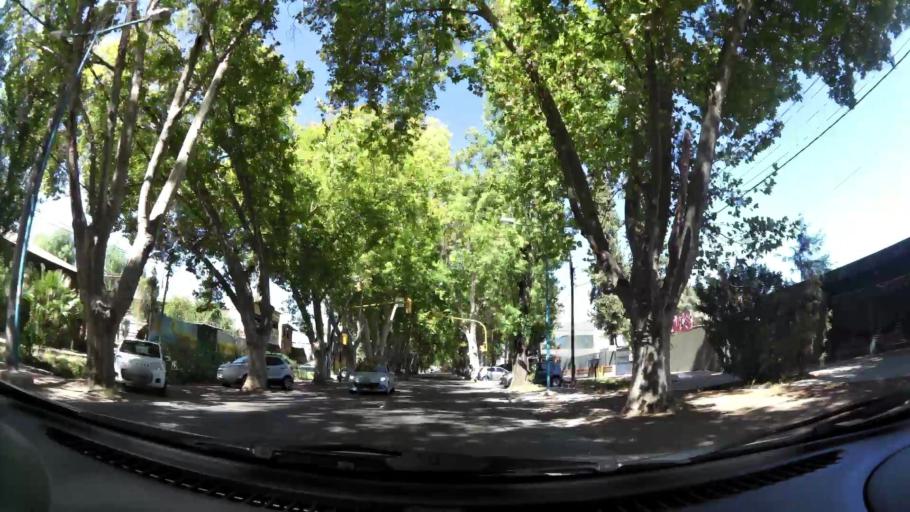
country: AR
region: Mendoza
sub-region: Departamento de Godoy Cruz
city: Godoy Cruz
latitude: -32.9508
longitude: -68.8453
